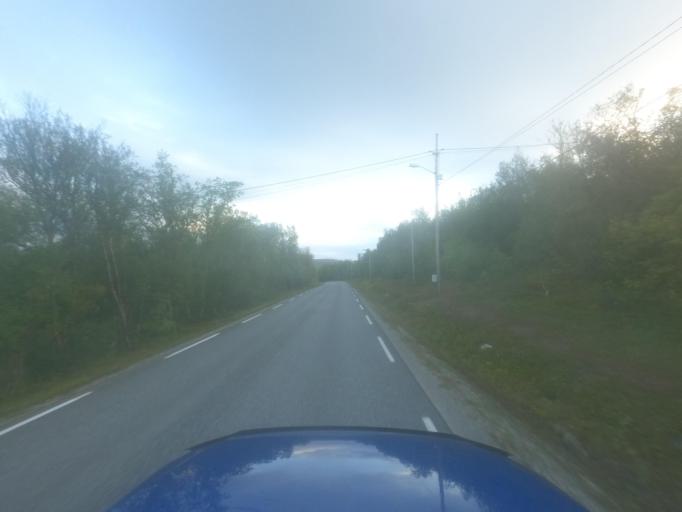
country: NO
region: Finnmark Fylke
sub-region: Porsanger
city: Lakselv
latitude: 70.3539
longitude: 25.0378
